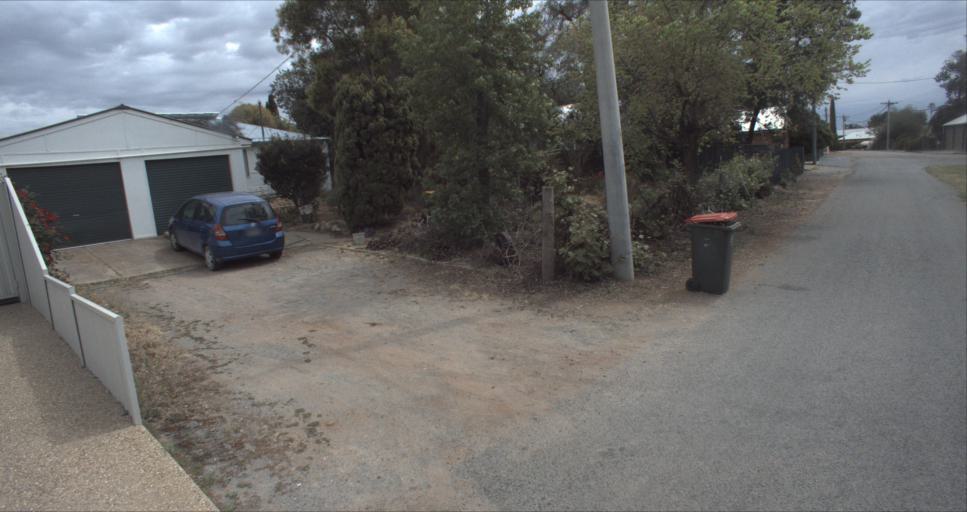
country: AU
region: New South Wales
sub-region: Leeton
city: Leeton
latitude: -34.5530
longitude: 146.4101
